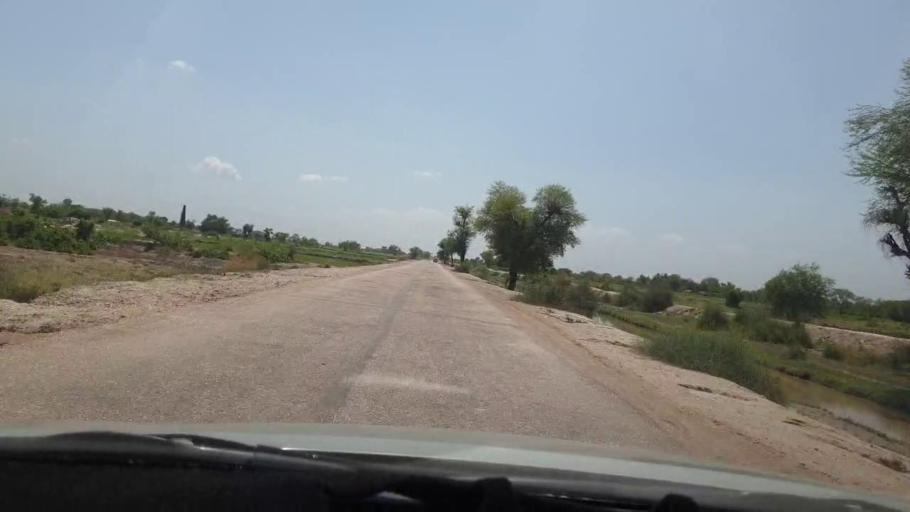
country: PK
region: Sindh
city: Pano Aqil
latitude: 27.7239
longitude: 69.1777
